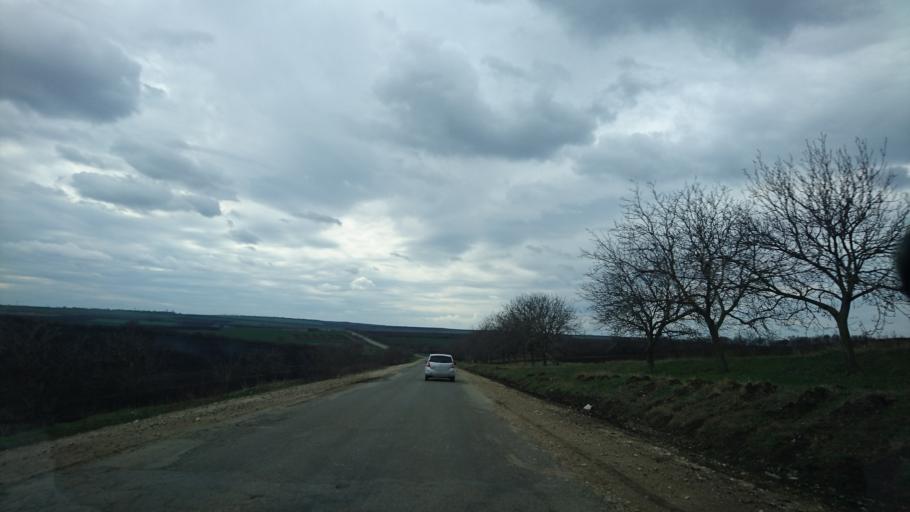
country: MD
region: Gagauzia
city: Comrat
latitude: 46.3101
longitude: 28.5931
